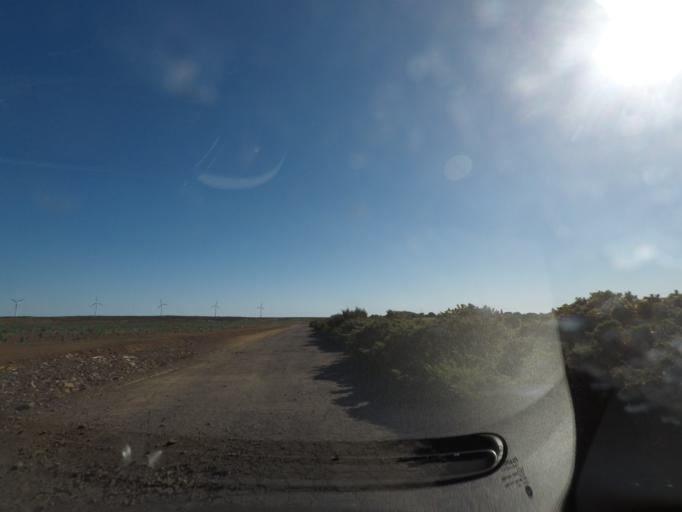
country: PT
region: Madeira
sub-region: Calheta
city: Arco da Calheta
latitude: 32.7593
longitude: -17.1014
